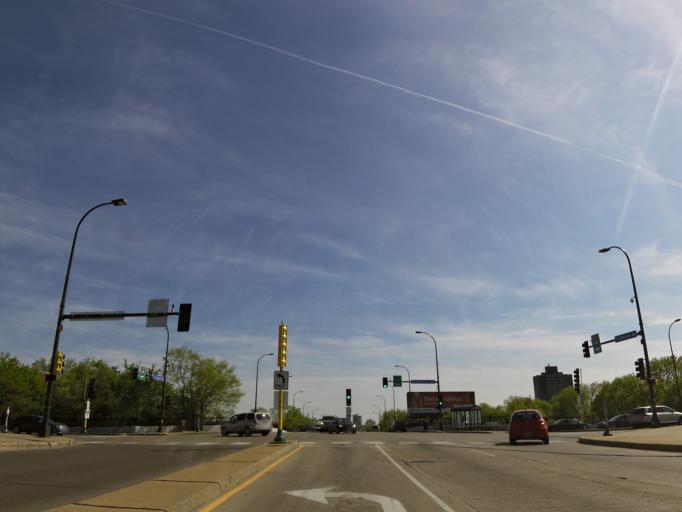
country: US
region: Minnesota
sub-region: Hennepin County
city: Minneapolis
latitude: 44.9991
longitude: -93.2473
